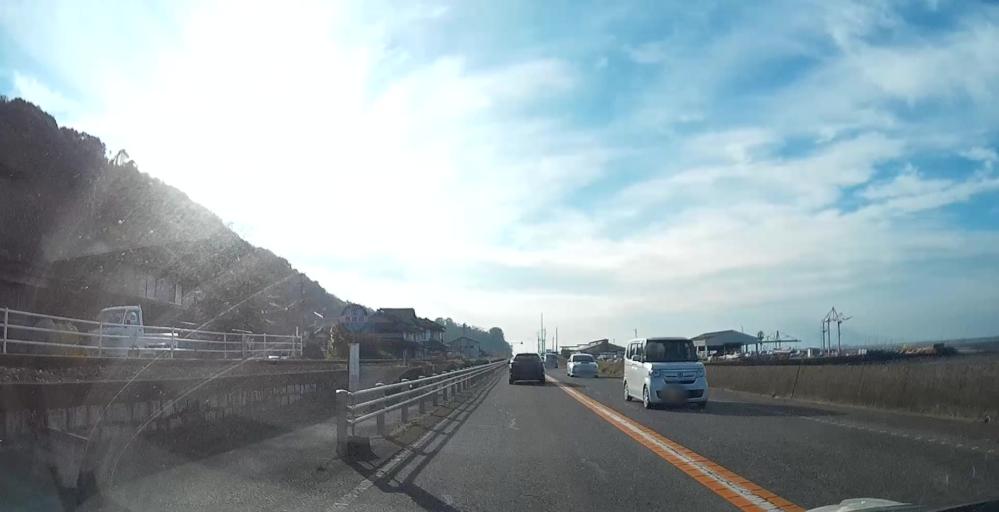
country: JP
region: Kumamoto
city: Uto
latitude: 32.7038
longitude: 130.5849
